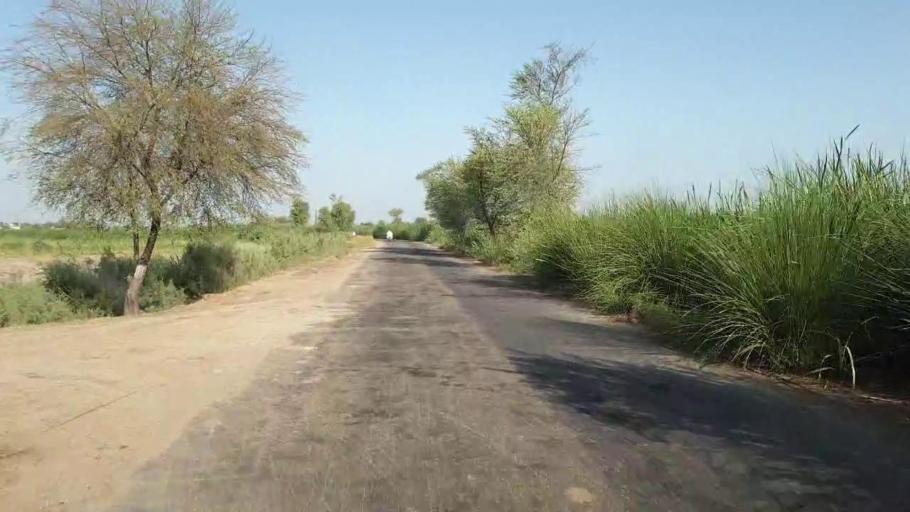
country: PK
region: Sindh
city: Nawabshah
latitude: 26.3765
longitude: 68.4627
